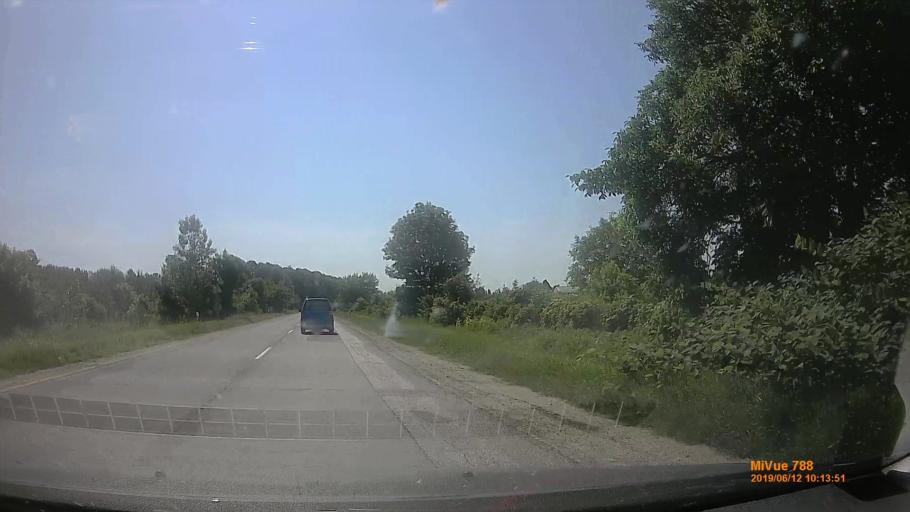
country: HU
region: Pest
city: Dabas
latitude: 47.2155
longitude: 19.2781
